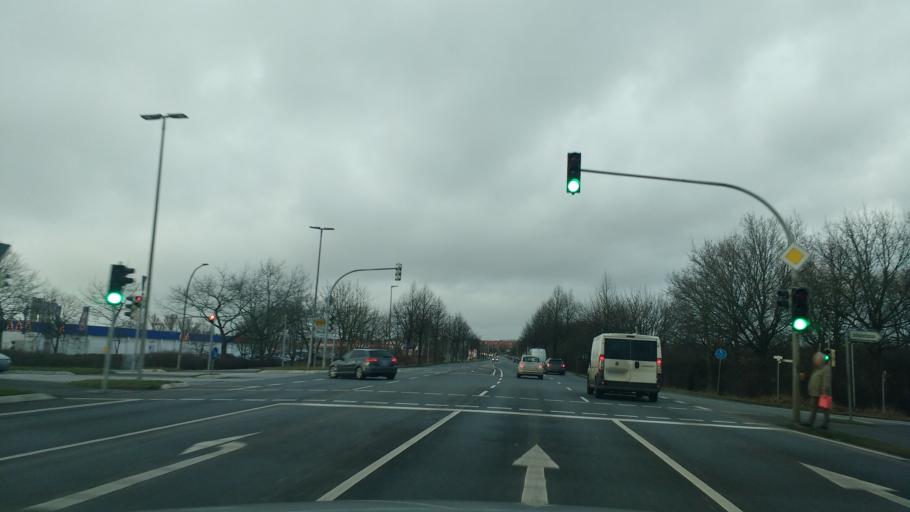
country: DE
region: Schleswig-Holstein
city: Itzehoe
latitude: 53.9128
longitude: 9.5161
